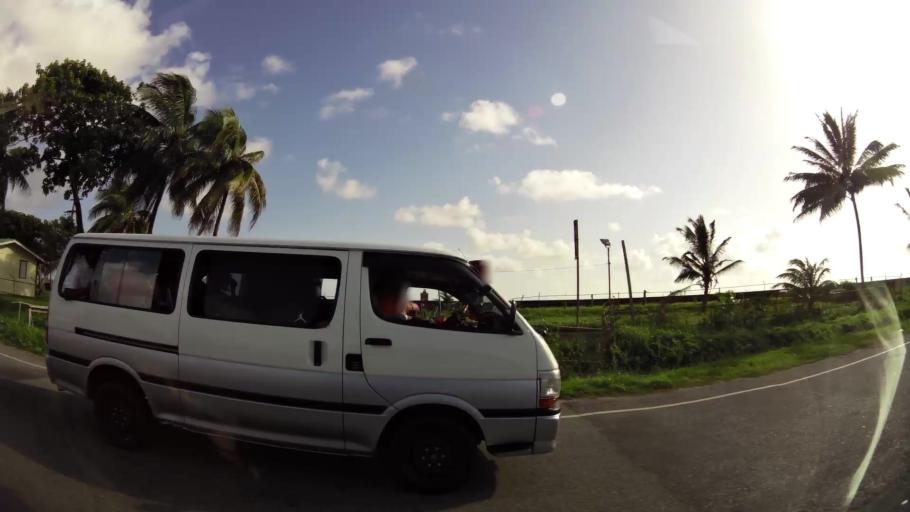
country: GY
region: Demerara-Mahaica
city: Georgetown
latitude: 6.8259
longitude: -58.1193
